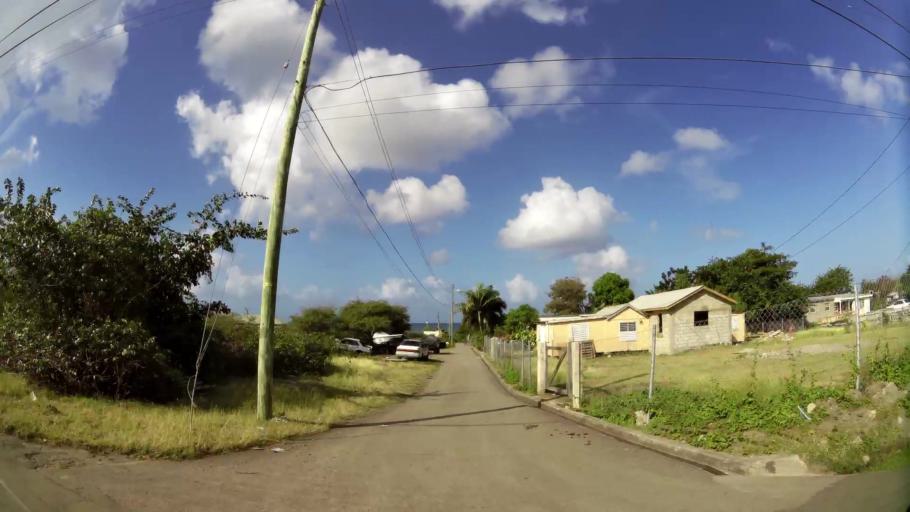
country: KN
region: Saint Paul Charlestown
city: Charlestown
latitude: 17.1263
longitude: -62.6265
